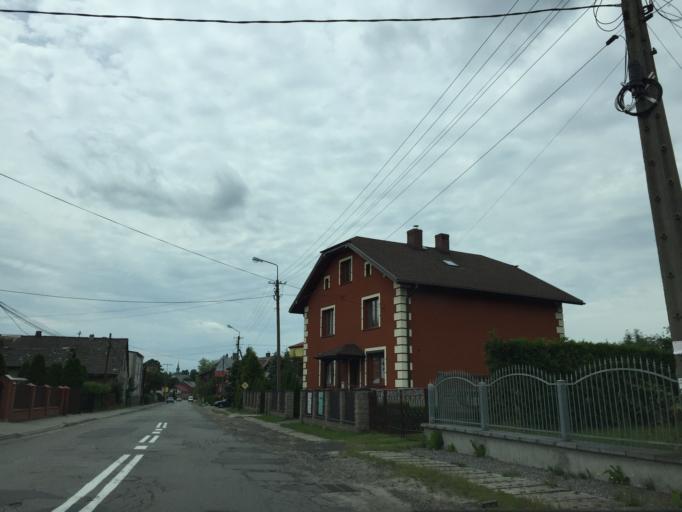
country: PL
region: Lesser Poland Voivodeship
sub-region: Powiat olkuski
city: Klucze
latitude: 50.3687
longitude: 19.5158
